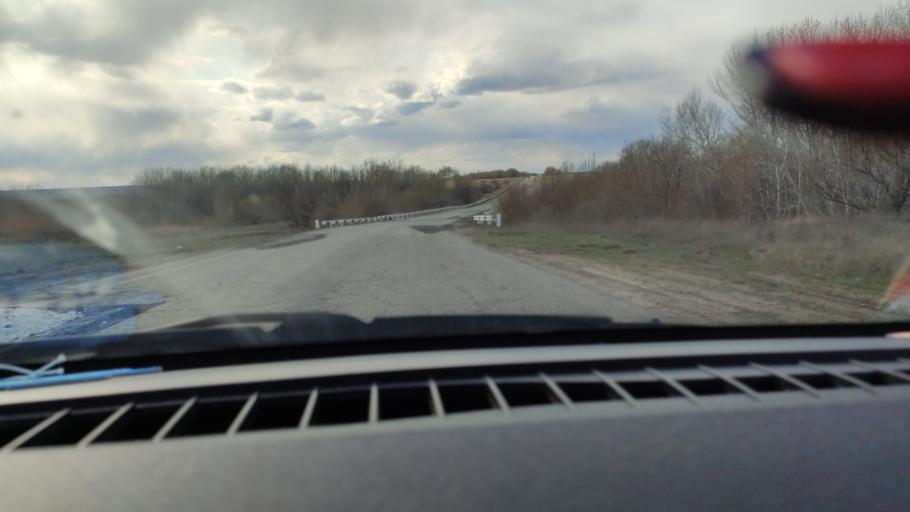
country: RU
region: Saratov
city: Rovnoye
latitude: 51.0486
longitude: 46.0472
